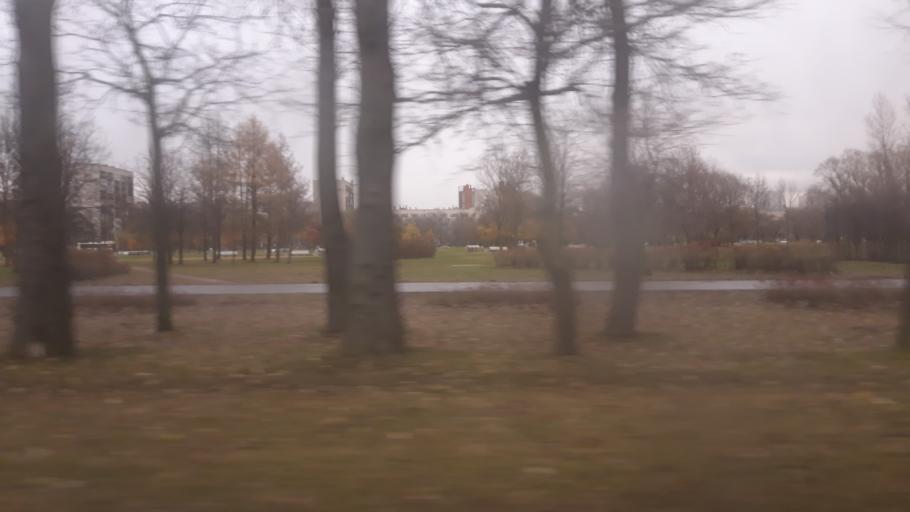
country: RU
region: St.-Petersburg
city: Kupchino
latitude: 59.8391
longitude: 30.3225
